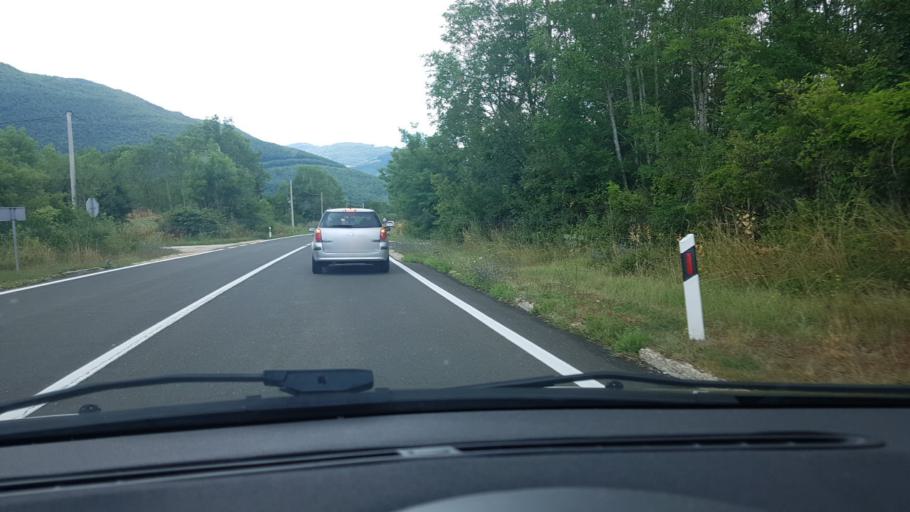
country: HR
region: Zadarska
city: Gracac
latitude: 44.2970
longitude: 15.8567
